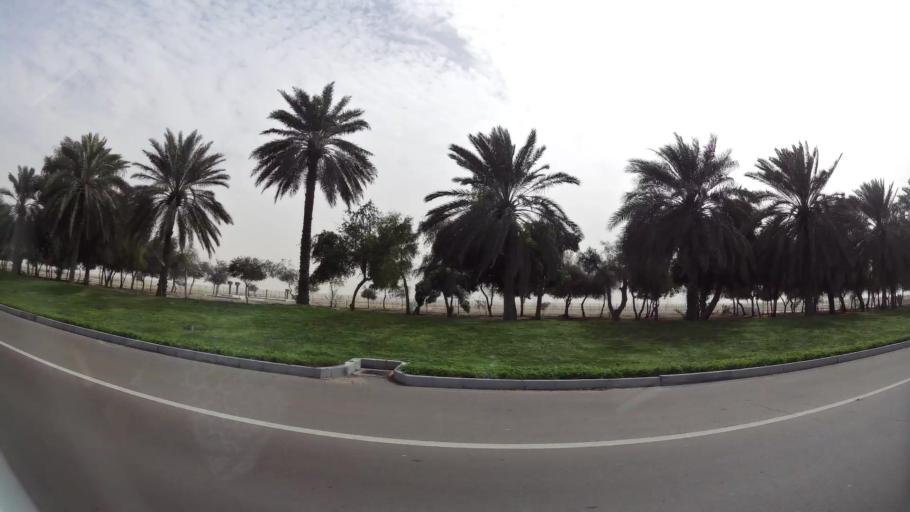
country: AE
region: Abu Dhabi
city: Abu Dhabi
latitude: 24.3936
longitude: 54.5550
